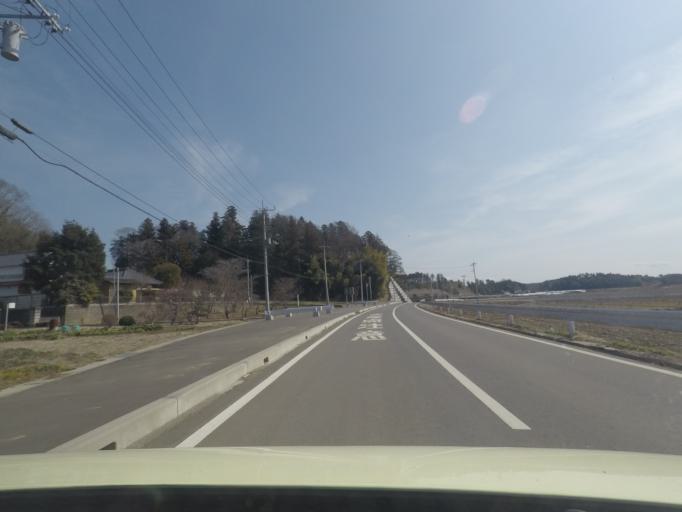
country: JP
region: Ibaraki
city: Ishioka
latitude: 36.1949
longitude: 140.3384
